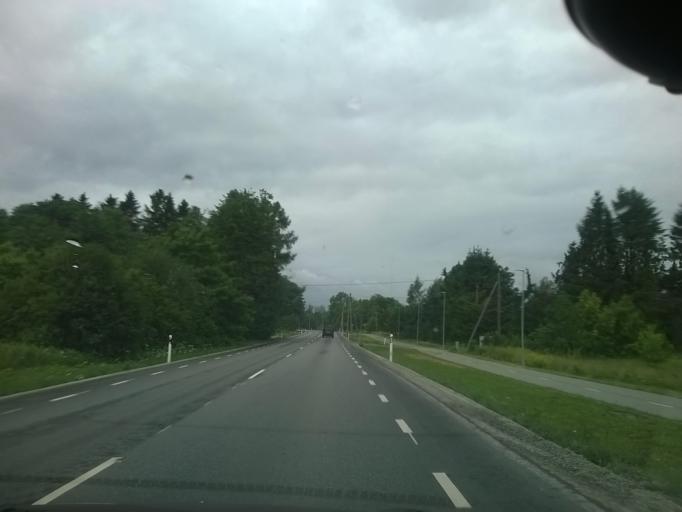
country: EE
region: Harju
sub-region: Rae vald
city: Jueri
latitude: 59.3681
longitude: 24.8694
